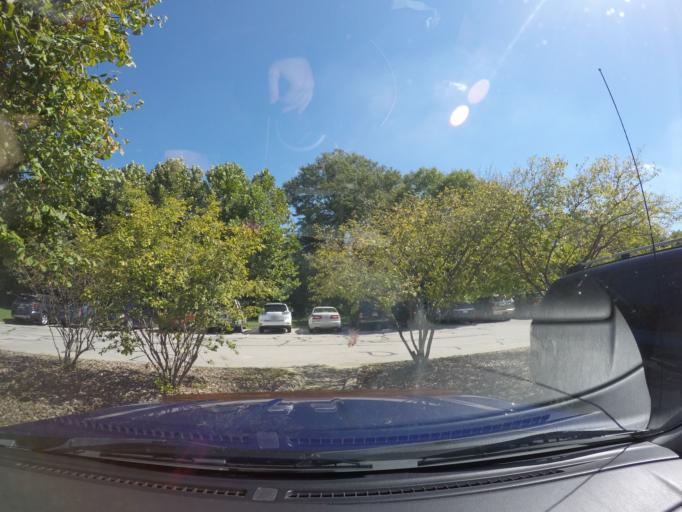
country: US
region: Kansas
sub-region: Johnson County
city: Leawood
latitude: 38.9324
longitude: -94.6144
